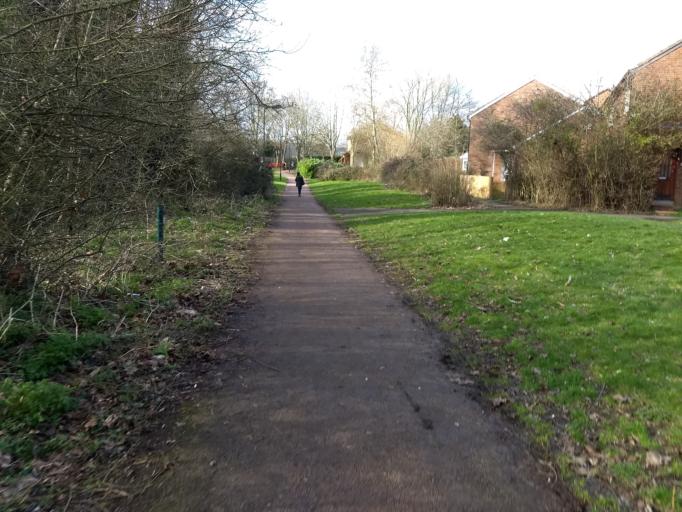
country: GB
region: England
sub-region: Milton Keynes
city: Milton Keynes
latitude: 52.0310
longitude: -0.7390
